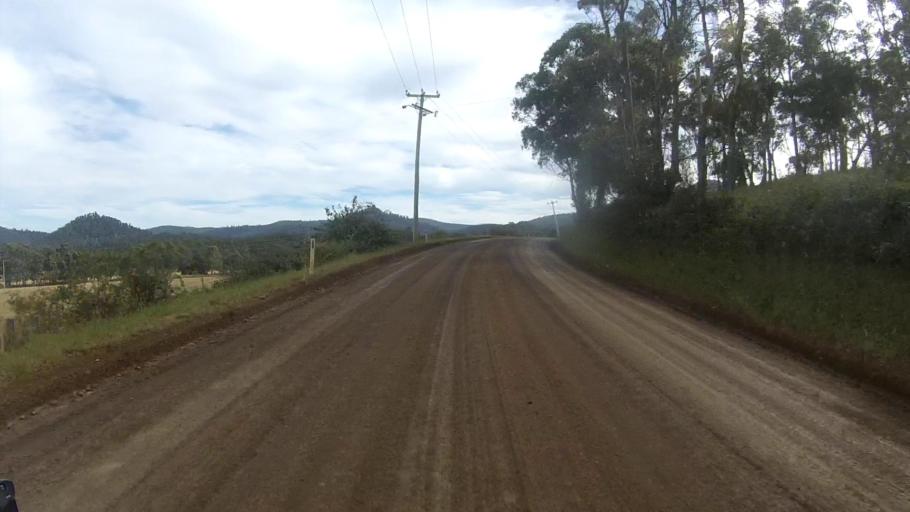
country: AU
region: Tasmania
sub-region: Sorell
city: Sorell
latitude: -42.7837
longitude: 147.8080
